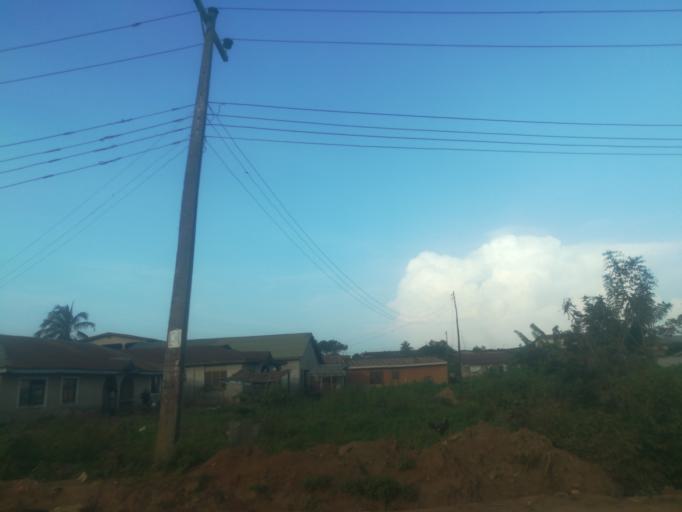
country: NG
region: Oyo
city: Moniya
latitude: 7.5373
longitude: 3.9011
